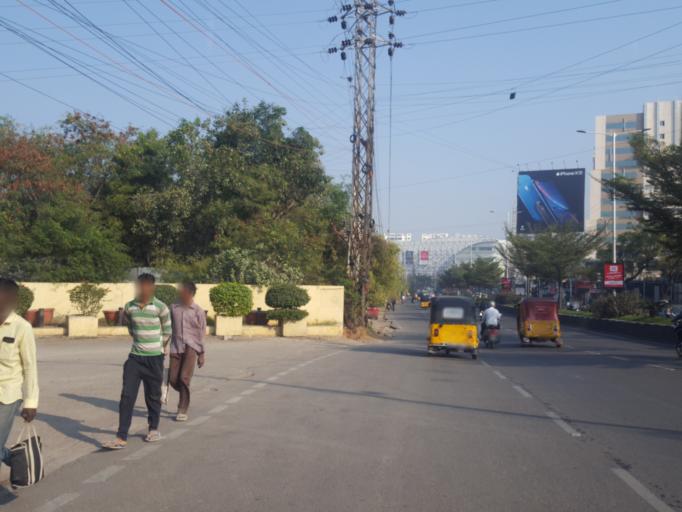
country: IN
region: Telangana
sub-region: Rangareddi
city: Kukatpalli
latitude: 17.4530
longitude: 78.3636
